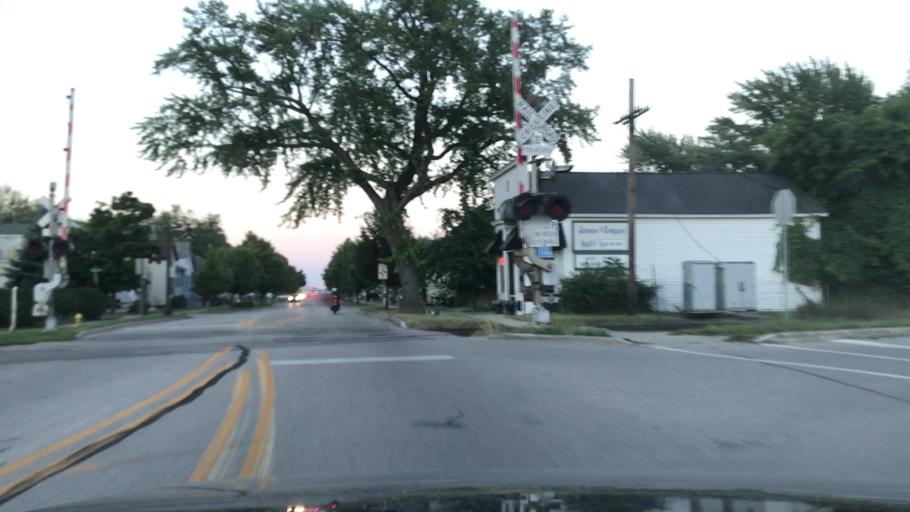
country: US
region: Michigan
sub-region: Ottawa County
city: Grand Haven
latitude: 43.0665
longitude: -86.2261
